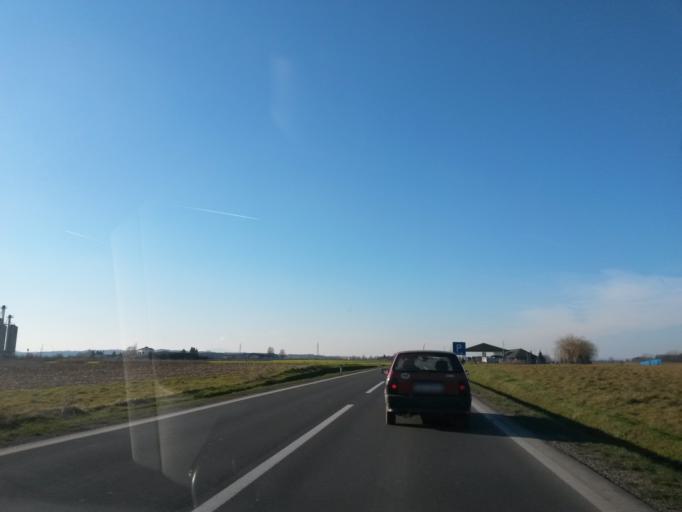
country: HR
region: Varazdinska
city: Ludbreg
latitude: 46.2583
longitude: 16.6095
